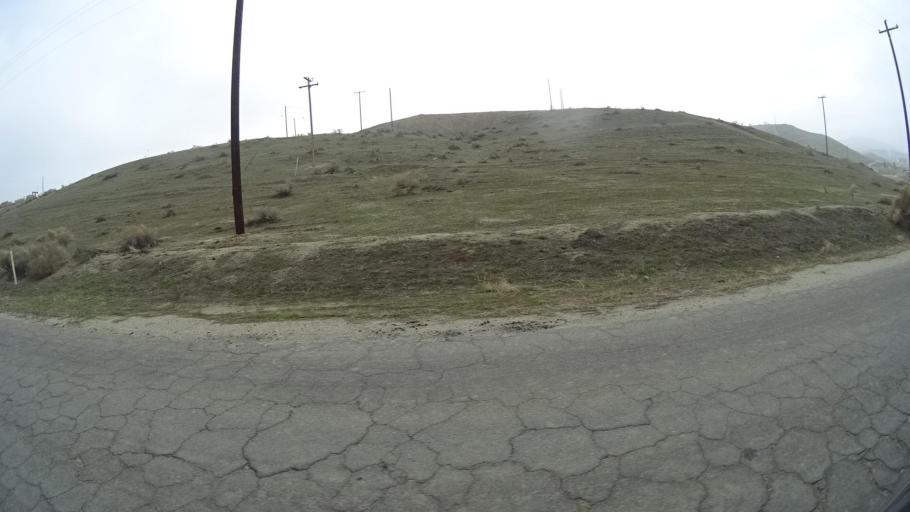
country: US
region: California
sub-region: Kern County
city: Maricopa
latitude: 35.0375
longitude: -119.3596
